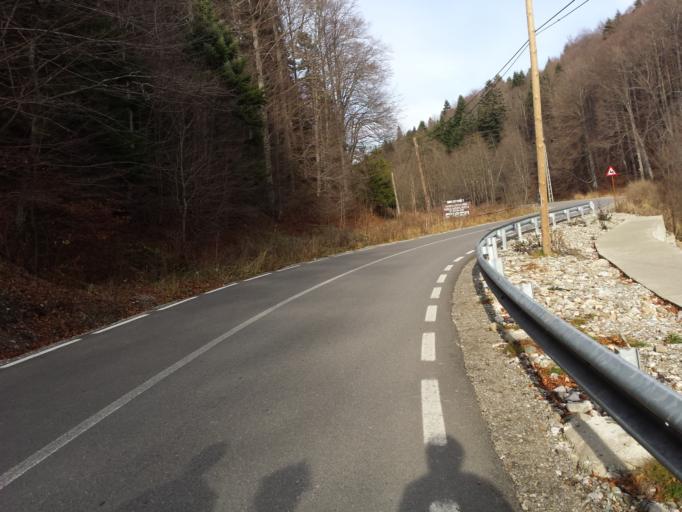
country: RO
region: Prahova
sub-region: Oras Azuga
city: Azuga
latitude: 45.4268
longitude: 25.5375
